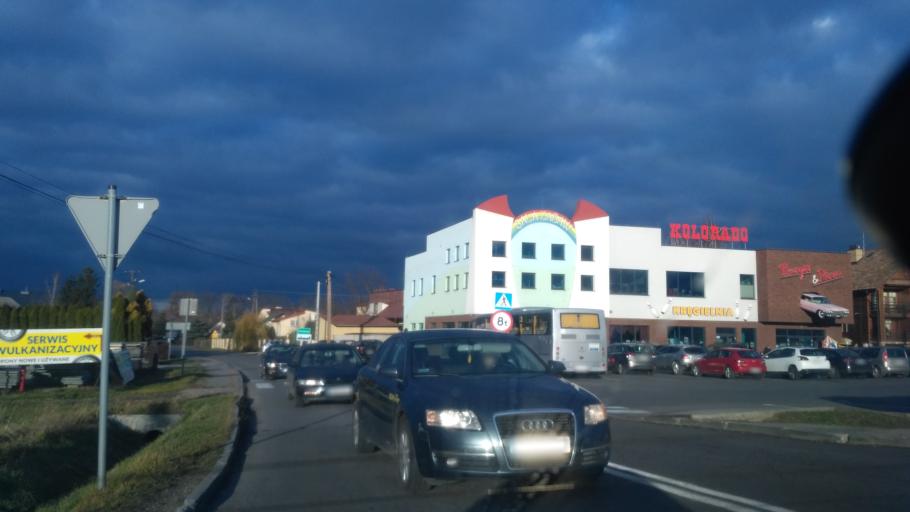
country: PL
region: Subcarpathian Voivodeship
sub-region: Powiat rzeszowski
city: Krasne
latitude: 50.0435
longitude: 22.1217
